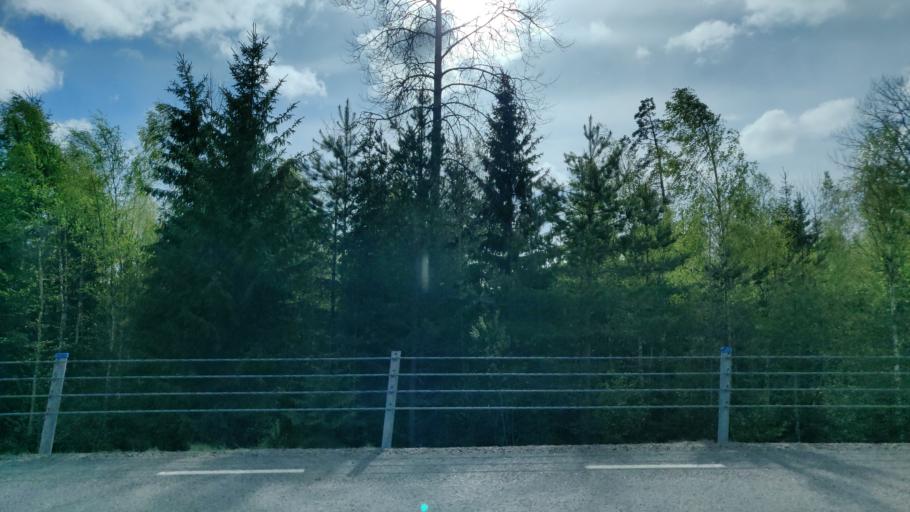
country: SE
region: Vaermland
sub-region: Forshaga Kommun
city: Deje
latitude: 59.5703
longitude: 13.4738
